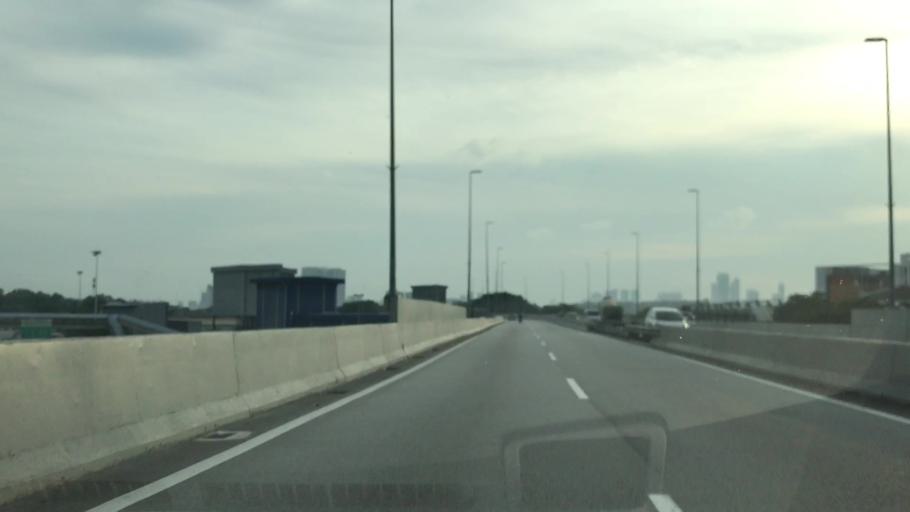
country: MY
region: Kuala Lumpur
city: Kuala Lumpur
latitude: 3.1143
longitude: 101.7158
